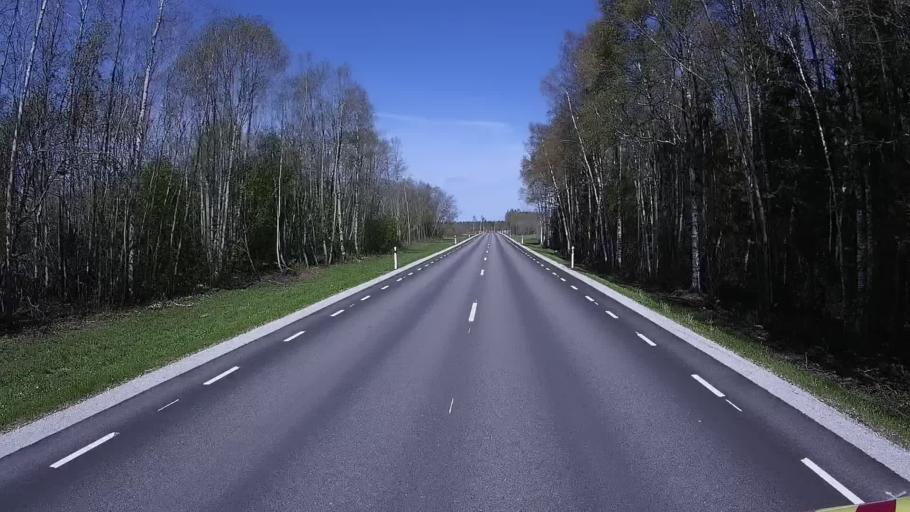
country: EE
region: Harju
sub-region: Nissi vald
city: Turba
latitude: 59.1663
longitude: 24.0743
